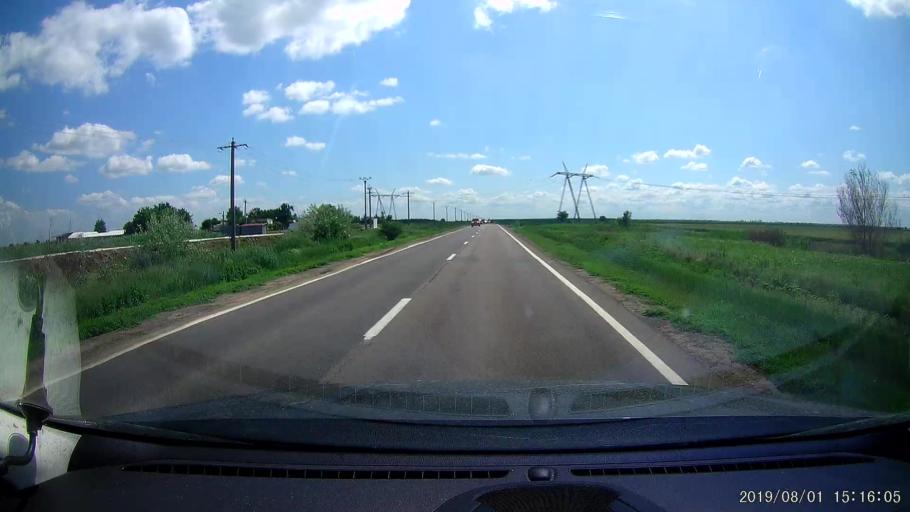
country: RO
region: Braila
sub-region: Comuna Tichilesti
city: Tichilesti
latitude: 45.1540
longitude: 27.8590
